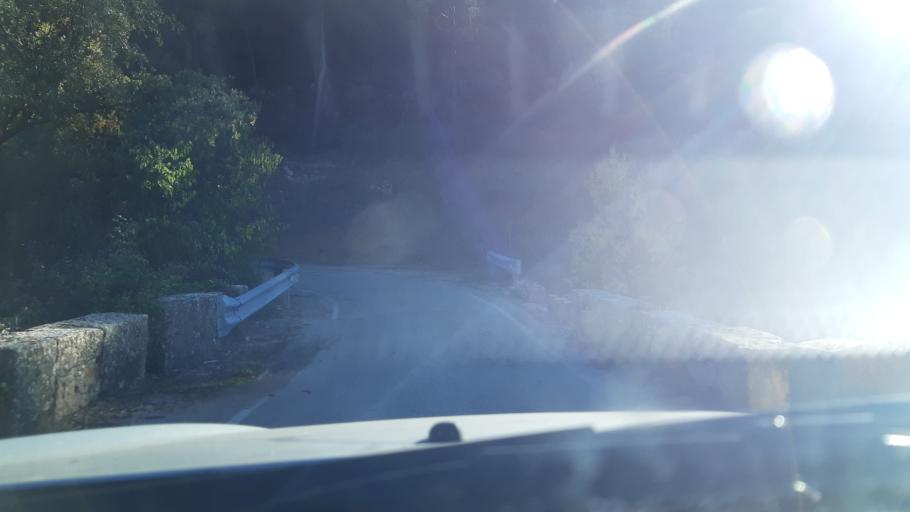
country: ES
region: Aragon
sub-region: Provincia de Teruel
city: Fornoles
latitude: 40.8991
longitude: -0.0084
